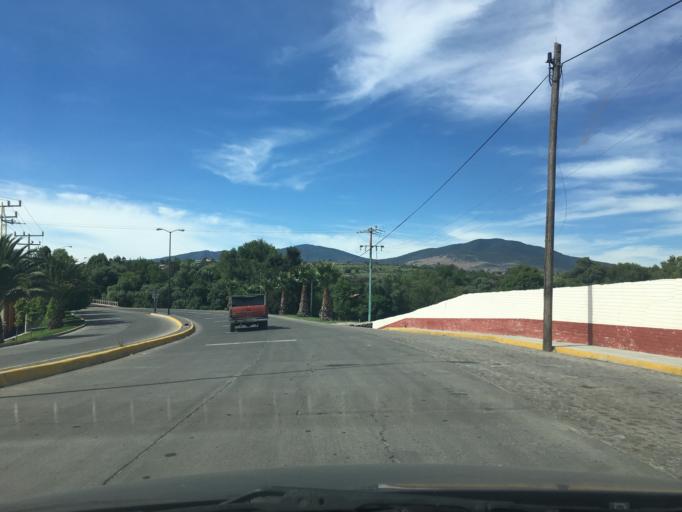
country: MX
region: Guanajuato
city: Coroneo
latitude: 20.1963
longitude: -100.3663
